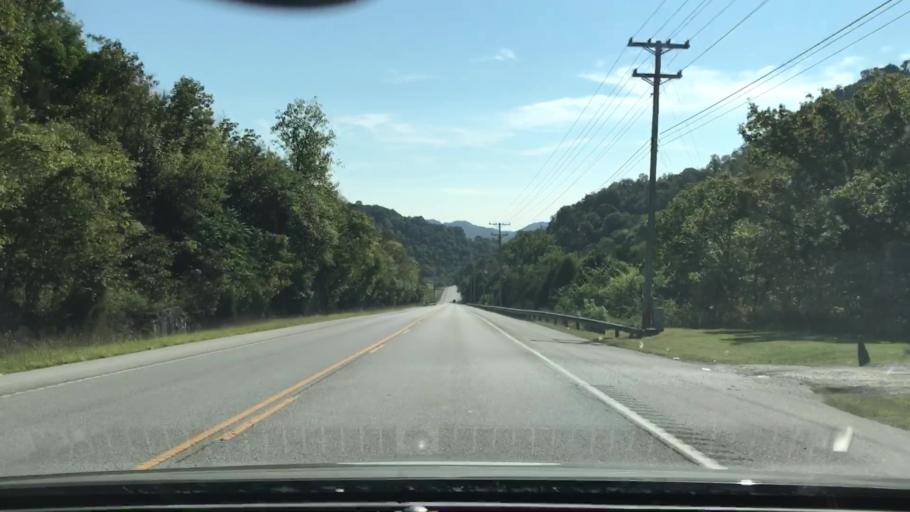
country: US
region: Tennessee
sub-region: Smith County
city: Carthage
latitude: 36.3231
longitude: -85.9351
